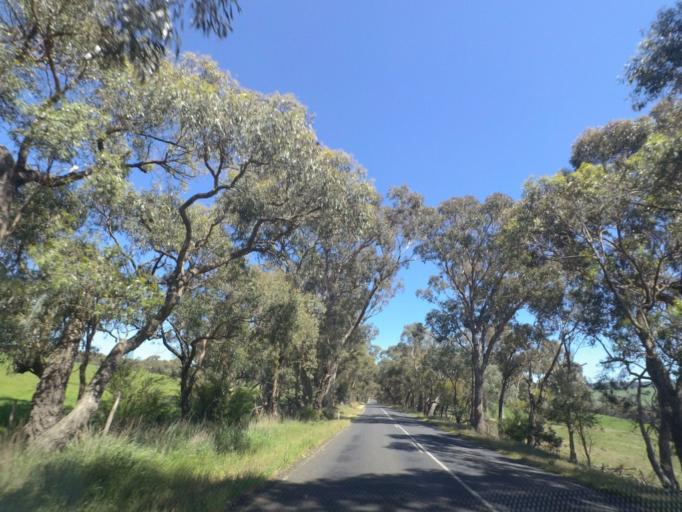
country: AU
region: Victoria
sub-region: Whittlesea
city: Whittlesea
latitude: -37.2658
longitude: 145.0435
